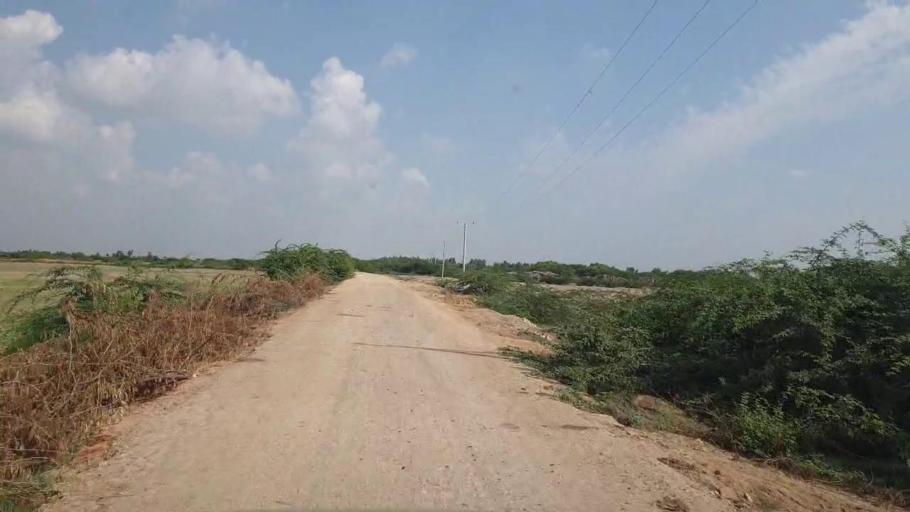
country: PK
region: Sindh
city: Badin
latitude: 24.4775
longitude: 68.6399
